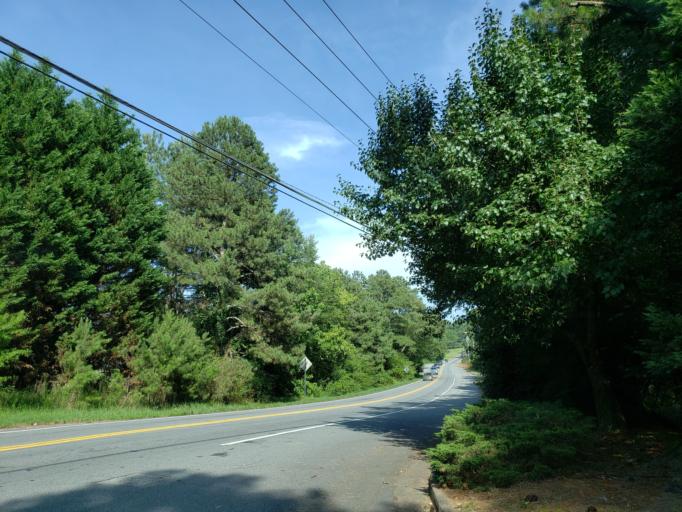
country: US
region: Georgia
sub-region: Cobb County
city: Mableton
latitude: 33.8677
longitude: -84.6069
